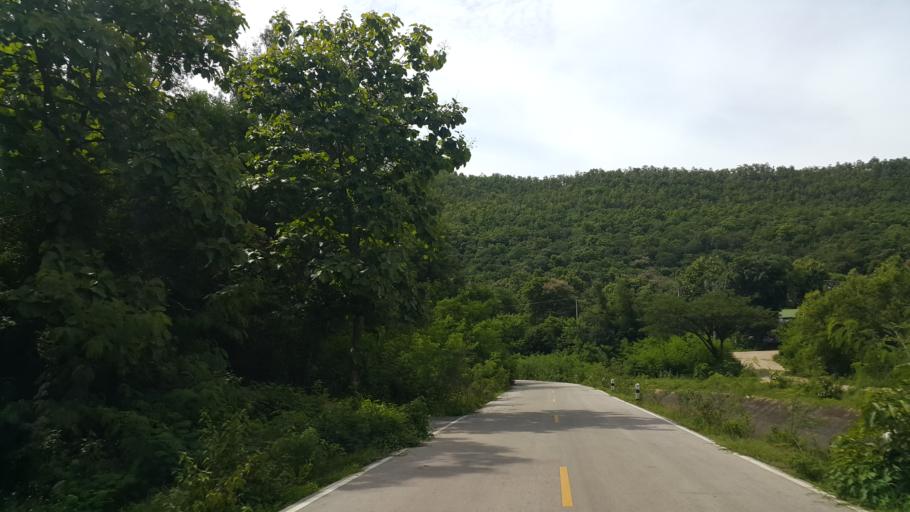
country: TH
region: Chiang Mai
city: Mae On
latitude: 18.7452
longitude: 99.2002
